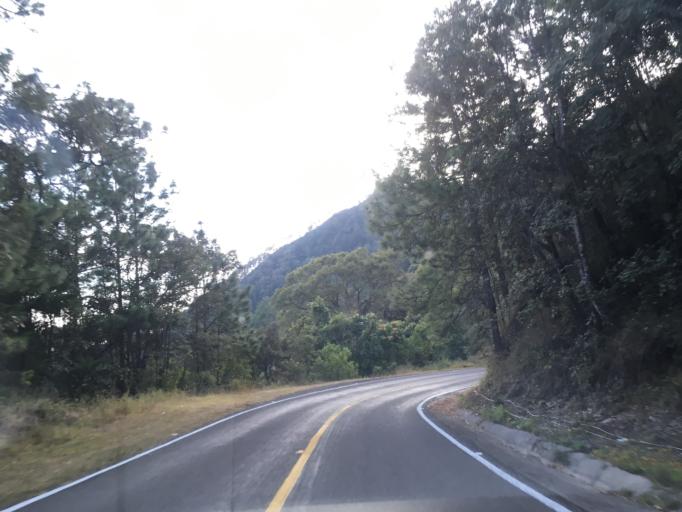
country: MX
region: Michoacan
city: Tzitzio
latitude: 19.6687
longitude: -100.9231
